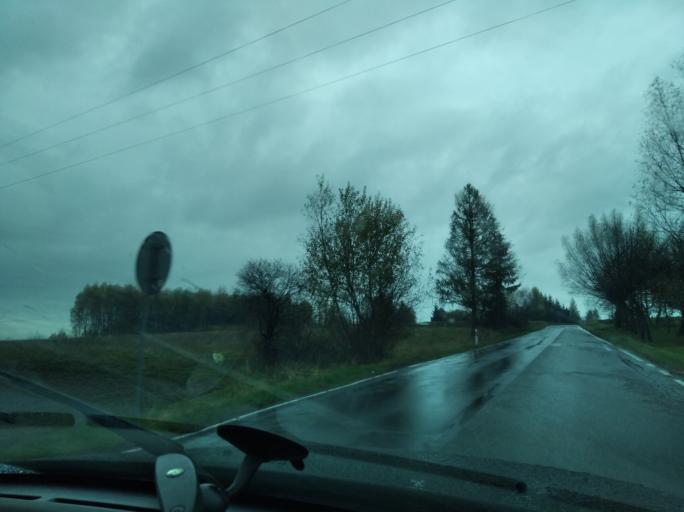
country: PL
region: Subcarpathian Voivodeship
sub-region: Powiat lancucki
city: Handzlowka
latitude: 49.9859
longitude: 22.1907
